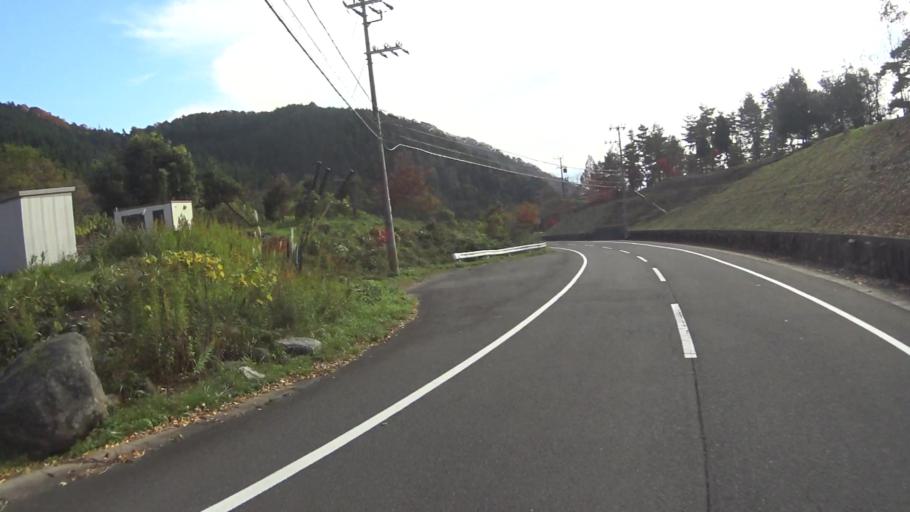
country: JP
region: Kyoto
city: Maizuru
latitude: 35.5370
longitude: 135.3971
